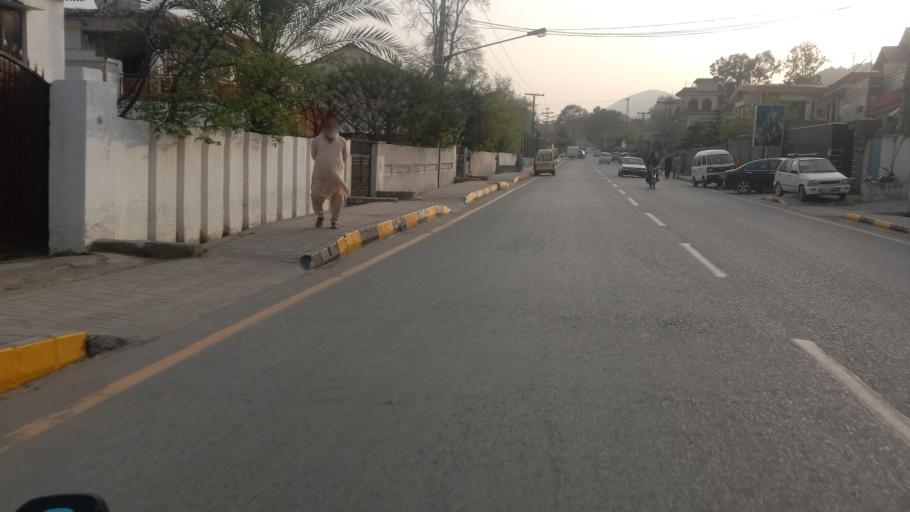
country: PK
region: Khyber Pakhtunkhwa
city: Abbottabad
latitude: 34.1672
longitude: 73.2276
